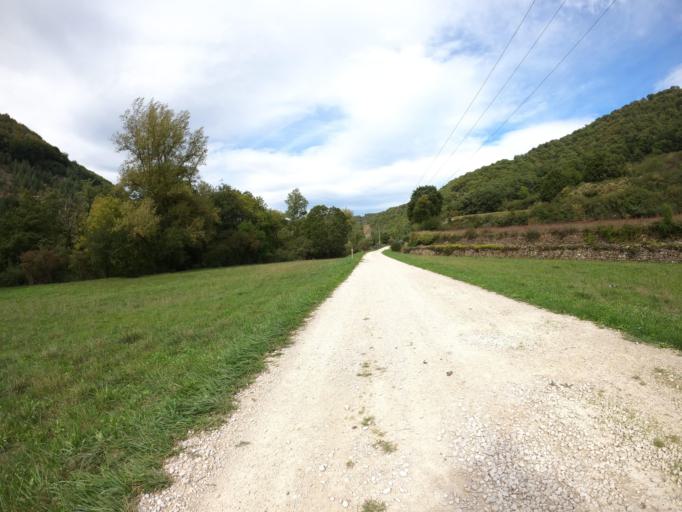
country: ES
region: Navarre
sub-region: Provincia de Navarra
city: Irurtzun
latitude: 42.9568
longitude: -1.8240
